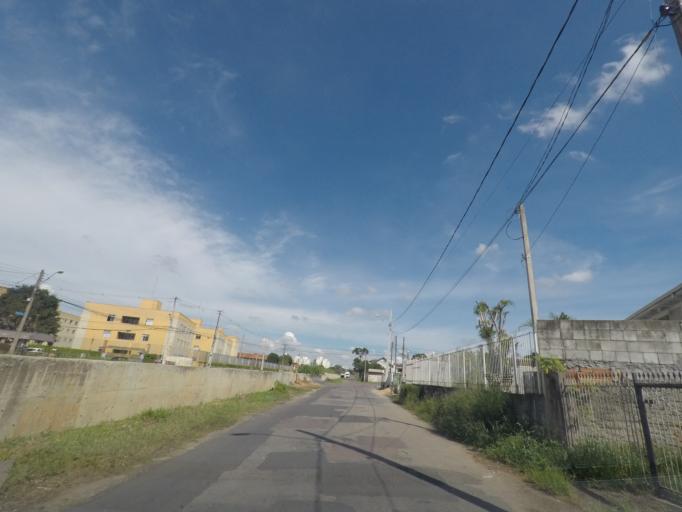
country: BR
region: Parana
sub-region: Curitiba
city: Curitiba
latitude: -25.4756
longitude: -49.2672
